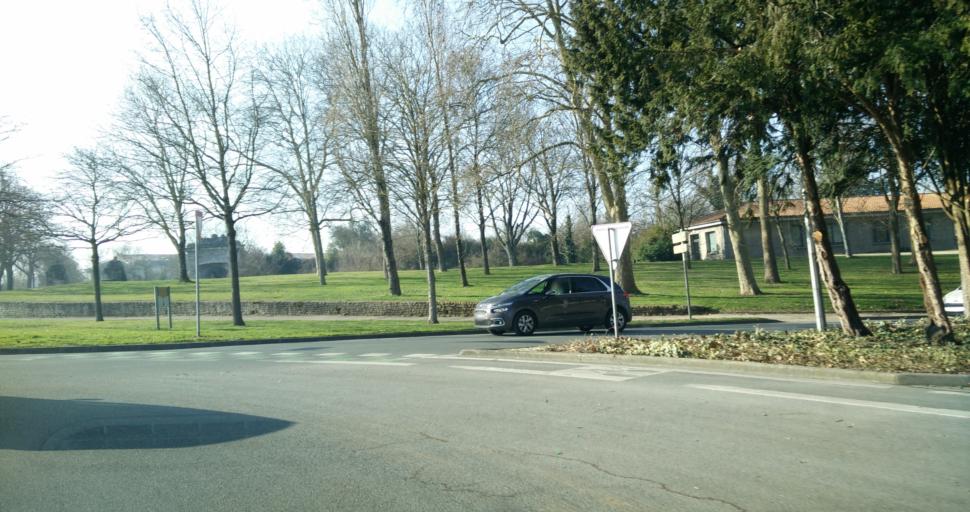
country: FR
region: Poitou-Charentes
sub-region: Departement de la Charente-Maritime
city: La Rochelle
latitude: 46.1691
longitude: -1.1500
